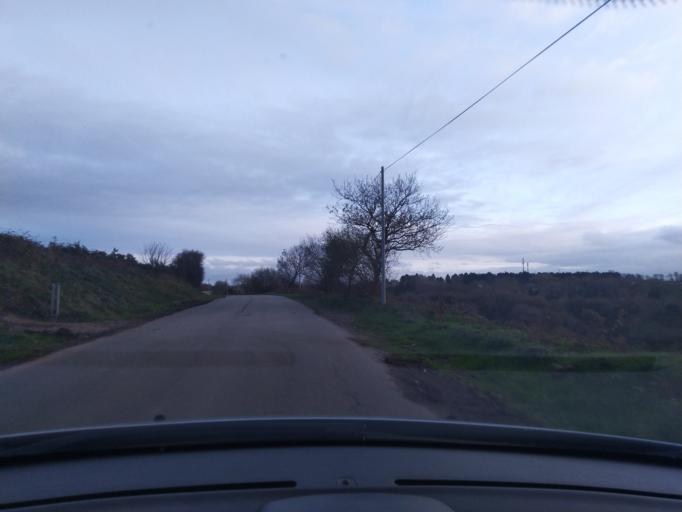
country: FR
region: Brittany
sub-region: Departement du Finistere
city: Guerlesquin
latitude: 48.5241
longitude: -3.6017
